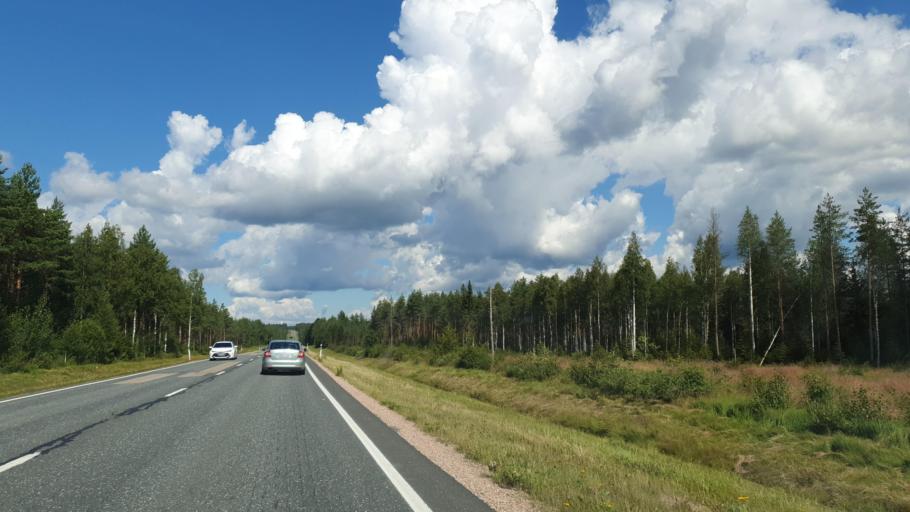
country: FI
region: Kainuu
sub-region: Kajaani
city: Kajaani
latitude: 64.0705
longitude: 27.4528
